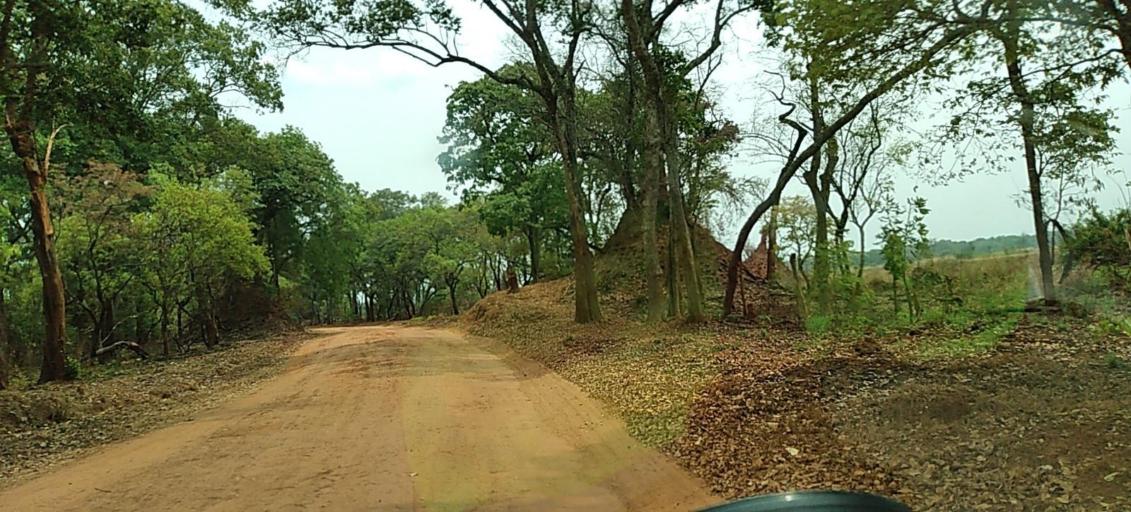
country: ZM
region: North-Western
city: Solwezi
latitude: -12.8115
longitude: 26.5371
